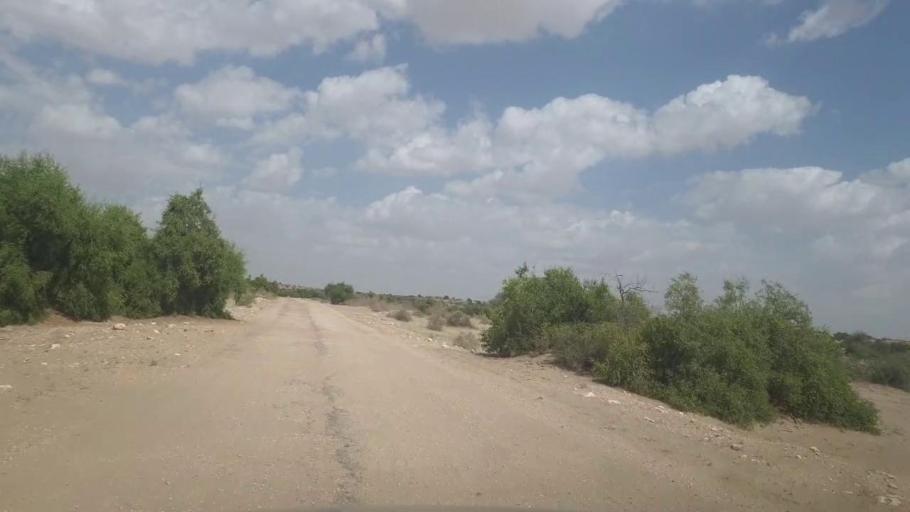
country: PK
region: Sindh
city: Kot Diji
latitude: 27.2712
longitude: 69.2050
